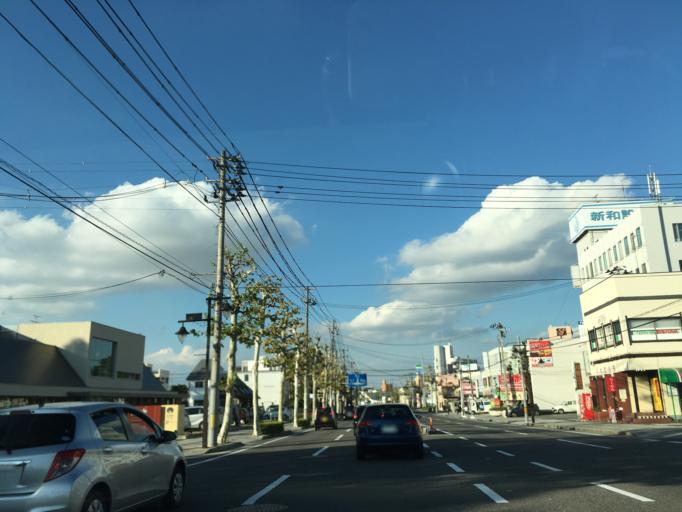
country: JP
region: Fukushima
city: Koriyama
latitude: 37.3977
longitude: 140.3629
